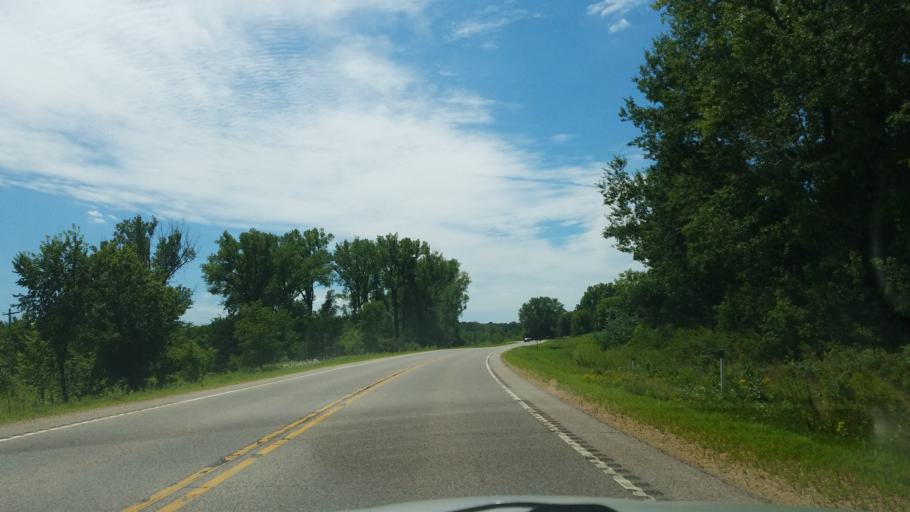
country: US
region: Wisconsin
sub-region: Saint Croix County
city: Glenwood City
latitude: 45.0386
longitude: -92.1780
